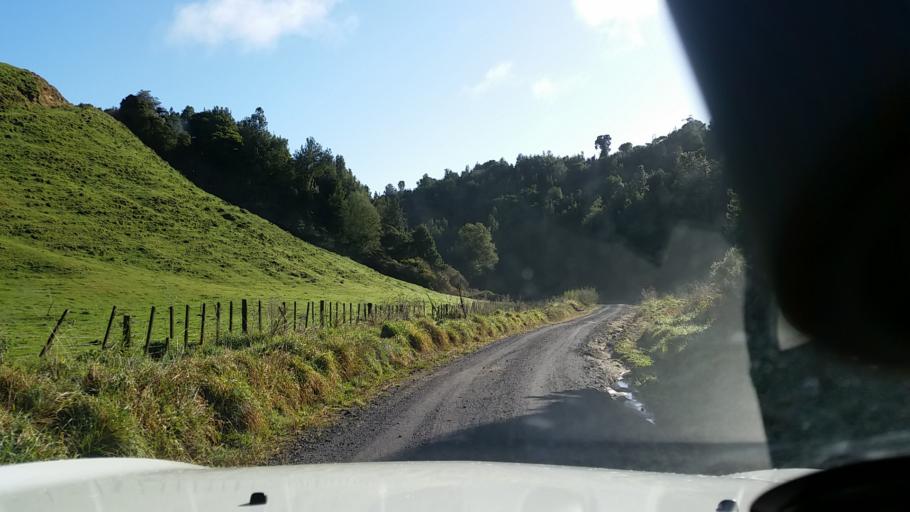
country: NZ
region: Bay of Plenty
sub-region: Kawerau District
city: Kawerau
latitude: -38.0106
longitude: 176.5659
